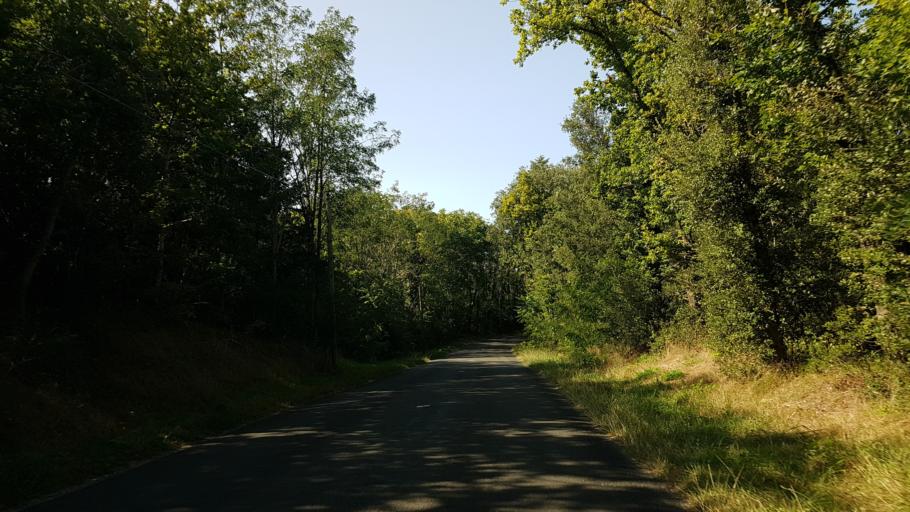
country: FR
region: Poitou-Charentes
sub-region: Departement de la Charente-Maritime
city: Saint-Palais-sur-Mer
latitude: 45.6638
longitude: -1.1203
